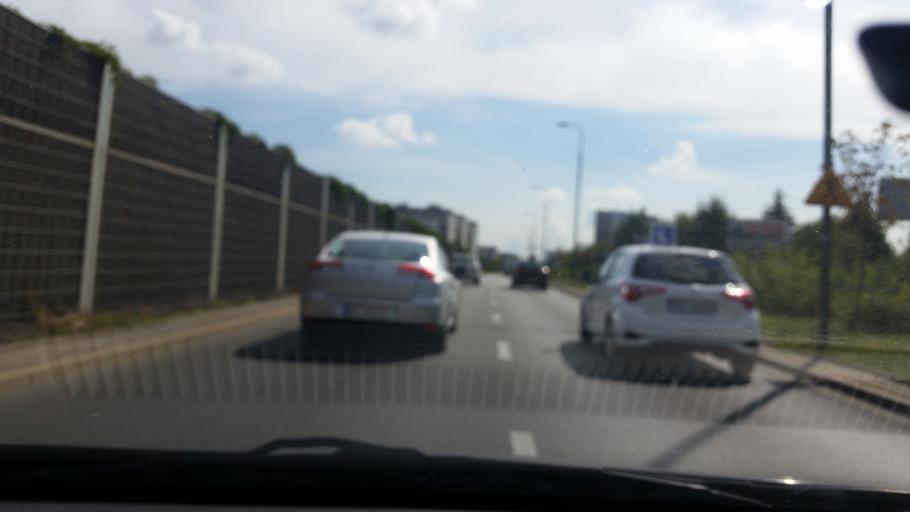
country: PL
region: Masovian Voivodeship
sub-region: Warszawa
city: Bielany
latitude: 52.2676
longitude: 20.9374
